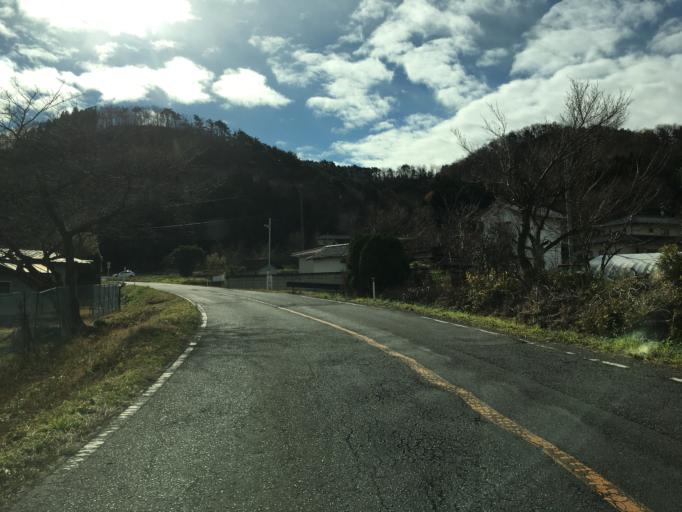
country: JP
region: Fukushima
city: Motomiya
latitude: 37.5192
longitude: 140.3693
